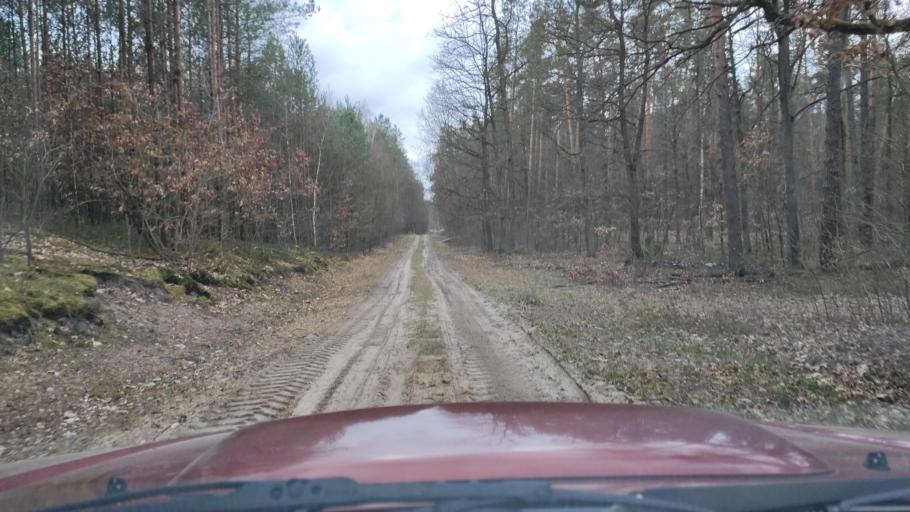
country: PL
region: Masovian Voivodeship
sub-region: Powiat kozienicki
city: Garbatka-Letnisko
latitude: 51.5092
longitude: 21.5484
